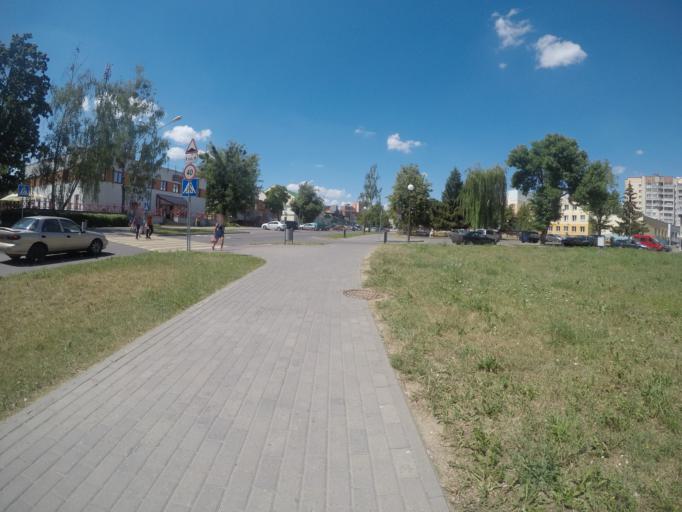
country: BY
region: Grodnenskaya
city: Hrodna
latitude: 53.6931
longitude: 23.8292
